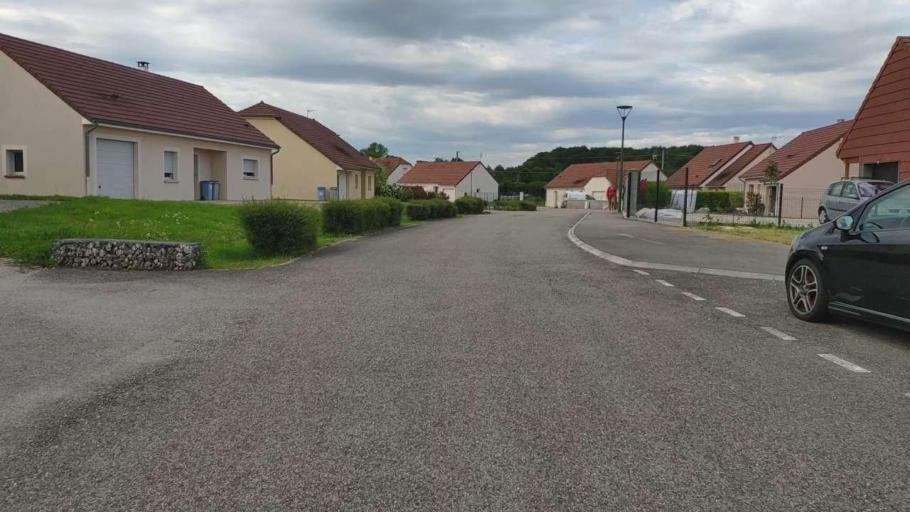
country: FR
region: Franche-Comte
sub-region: Departement du Jura
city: Perrigny
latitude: 46.7582
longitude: 5.6021
